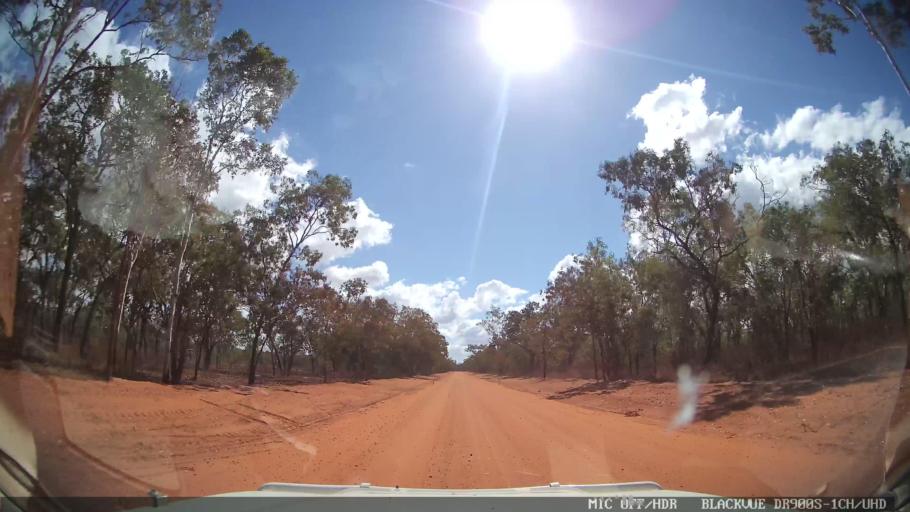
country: AU
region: Queensland
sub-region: Cook
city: Cooktown
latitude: -15.1959
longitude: 144.3804
